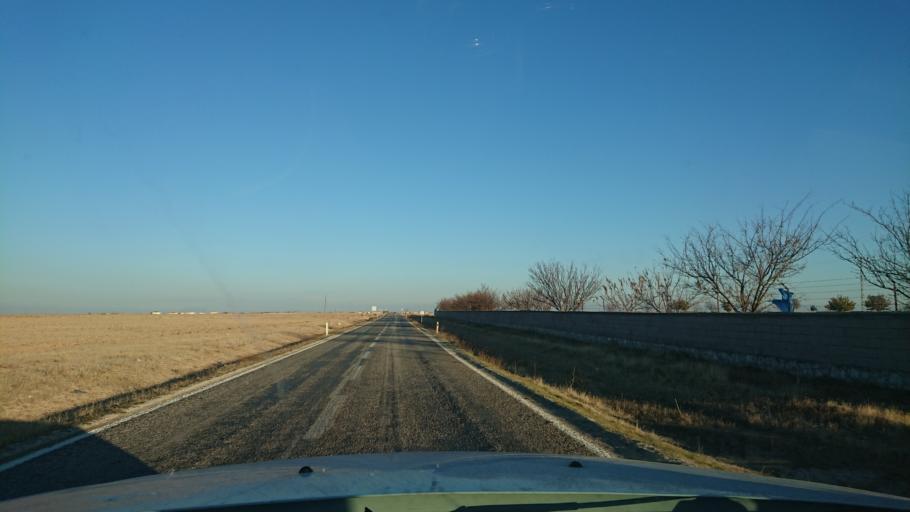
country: TR
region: Aksaray
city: Eskil
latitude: 38.4642
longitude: 33.2303
